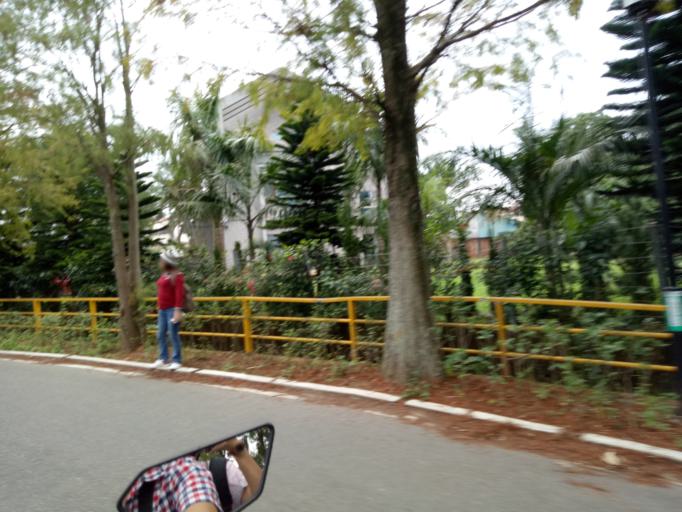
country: TW
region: Taiwan
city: Daxi
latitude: 24.8737
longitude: 121.2563
